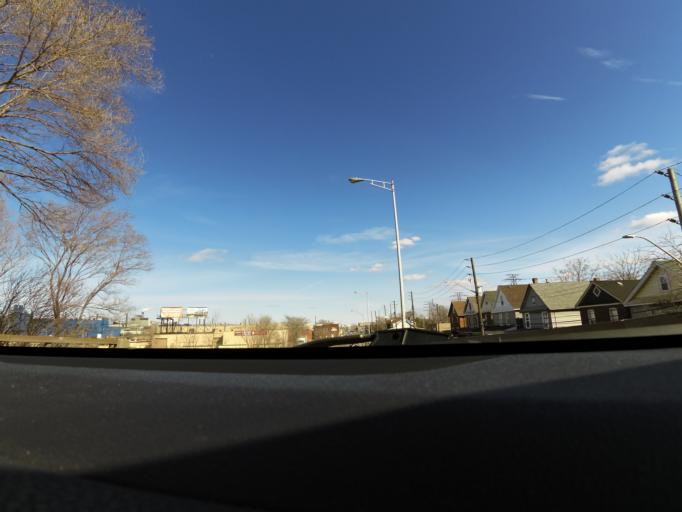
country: CA
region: Ontario
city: Hamilton
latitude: 43.2637
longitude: -79.8254
